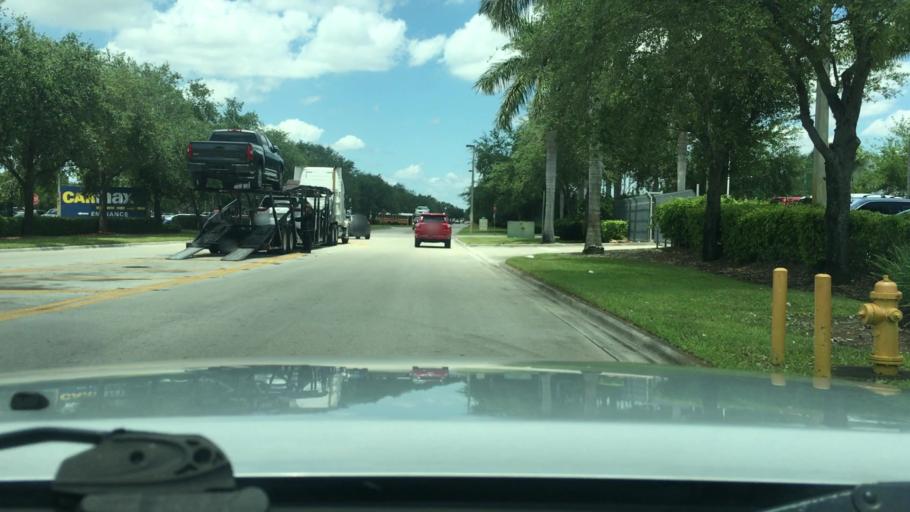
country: US
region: Florida
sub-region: Miami-Dade County
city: Fountainebleau
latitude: 25.7842
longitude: -80.3555
